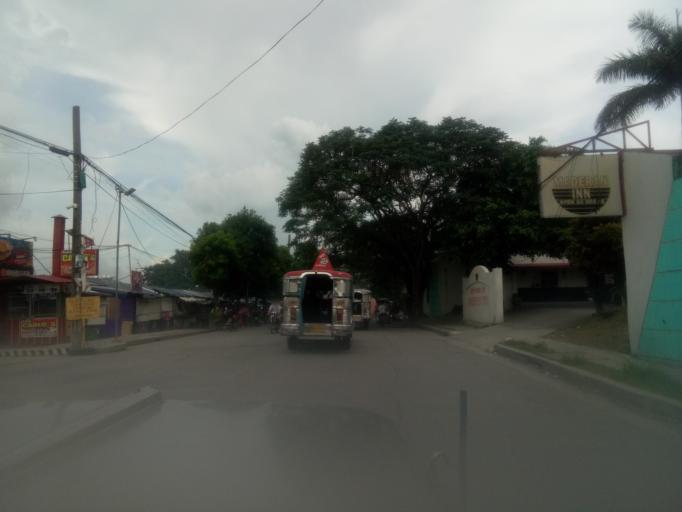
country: PH
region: Calabarzon
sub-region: Province of Cavite
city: Bulihan
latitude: 14.2867
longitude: 121.0002
